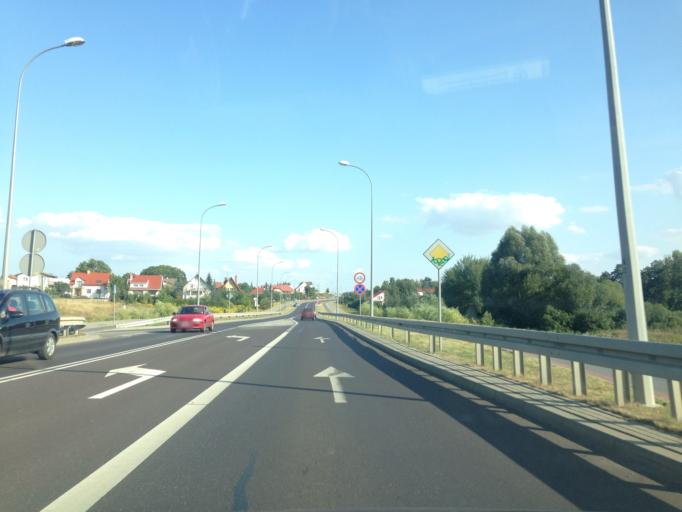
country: PL
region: Warmian-Masurian Voivodeship
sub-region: Powiat ilawski
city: Ilawa
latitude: 53.5995
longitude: 19.5721
